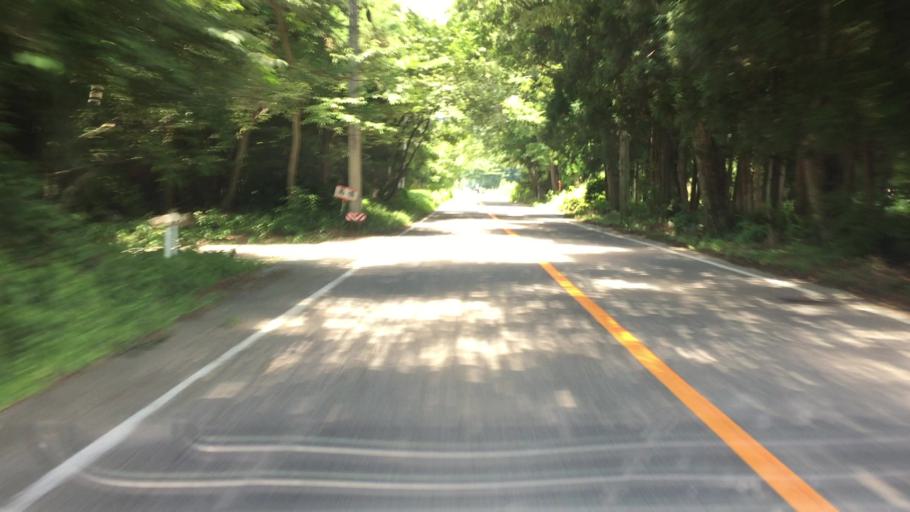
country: JP
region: Tochigi
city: Kuroiso
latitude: 37.0160
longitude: 139.9576
